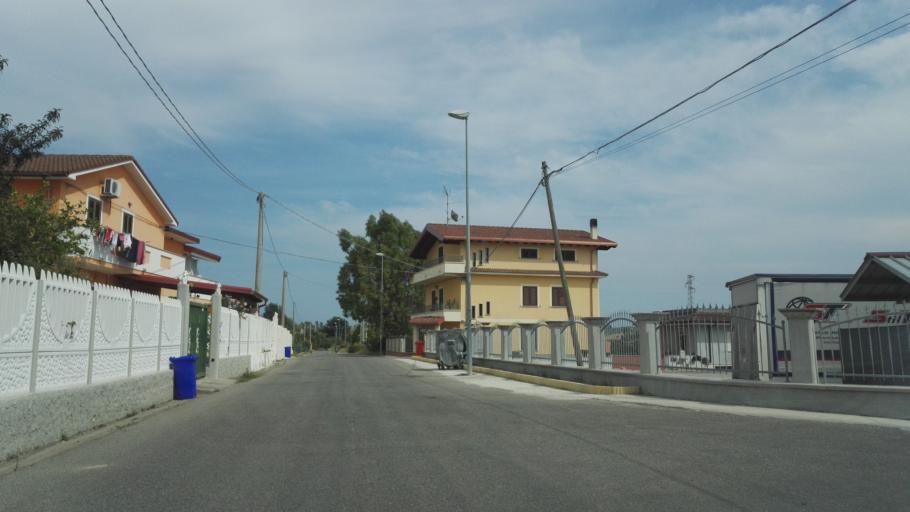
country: IT
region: Calabria
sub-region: Provincia di Reggio Calabria
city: Monasterace
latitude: 38.4304
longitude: 16.5350
